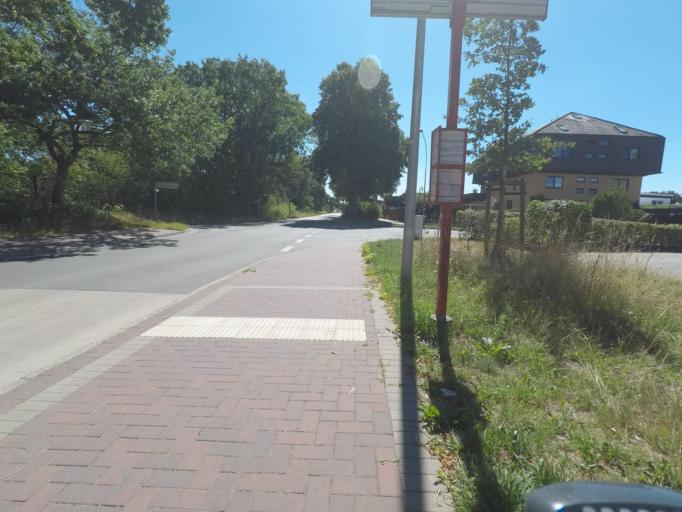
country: DE
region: Schleswig-Holstein
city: Trittau
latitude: 53.6252
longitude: 10.4022
